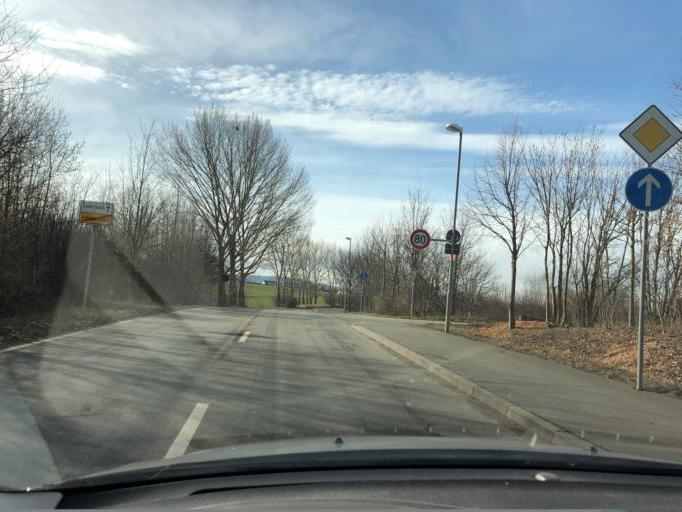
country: DE
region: Thuringia
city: Monchenholzhausen
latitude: 50.9856
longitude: 11.1060
